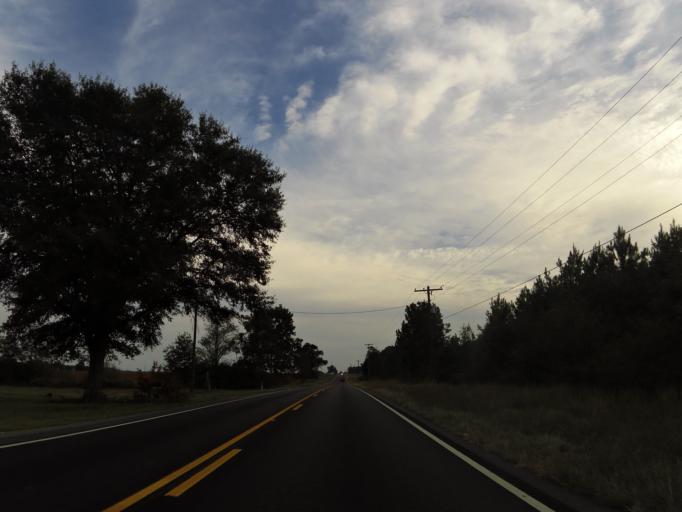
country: US
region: Alabama
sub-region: Escambia County
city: Atmore
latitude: 31.1845
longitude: -87.4638
